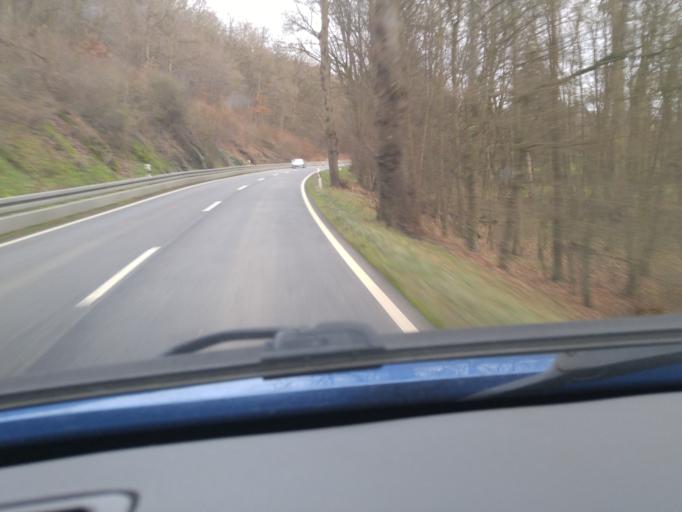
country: DE
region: Hesse
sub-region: Regierungsbezirk Darmstadt
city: Ober-Morlen
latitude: 50.3666
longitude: 8.6125
